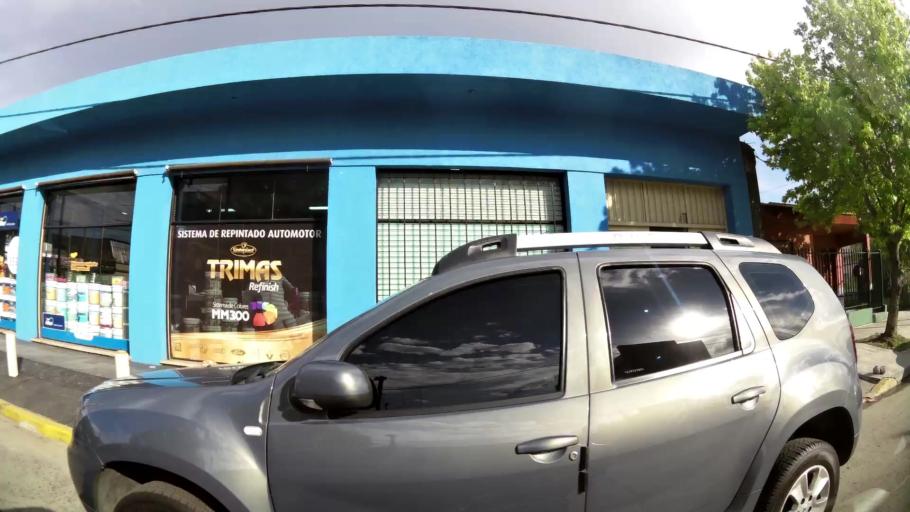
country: AR
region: Buenos Aires
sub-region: Partido de Lanus
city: Lanus
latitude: -34.6892
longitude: -58.3776
